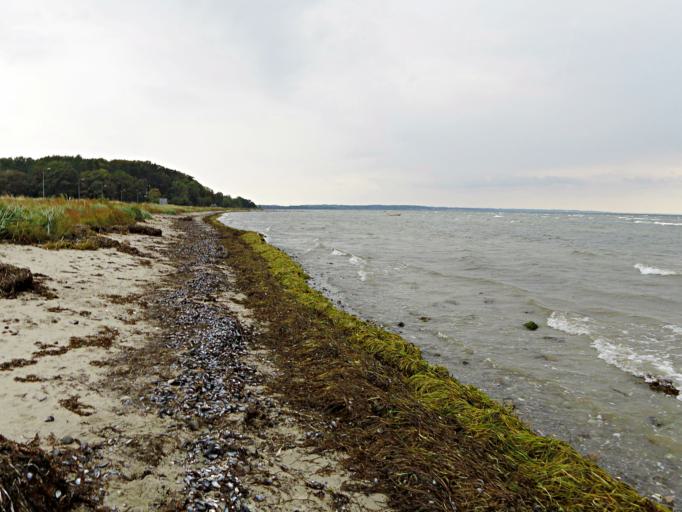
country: DK
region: Capital Region
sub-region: Fredensborg Kommune
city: Kokkedal
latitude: 55.9025
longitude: 12.5309
